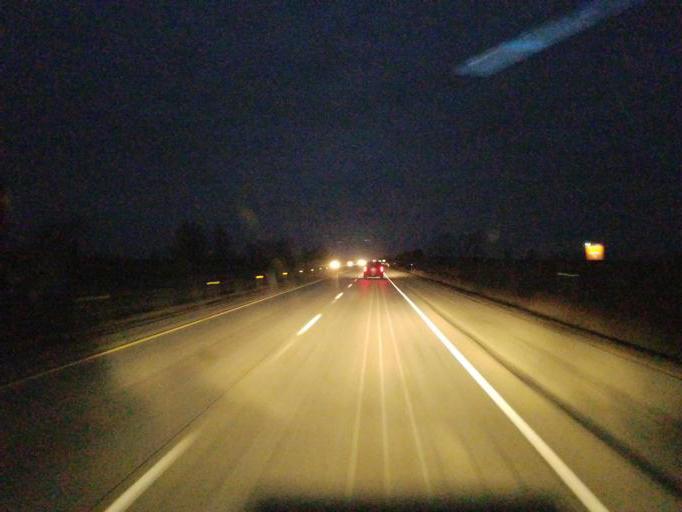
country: US
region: Iowa
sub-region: Guthrie County
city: Stuart
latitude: 41.4959
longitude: -94.4734
